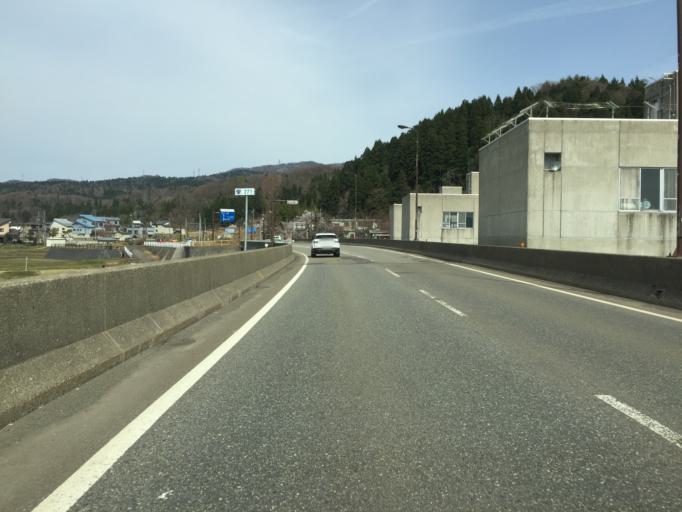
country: JP
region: Niigata
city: Ojiya
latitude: 37.3452
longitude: 138.8262
